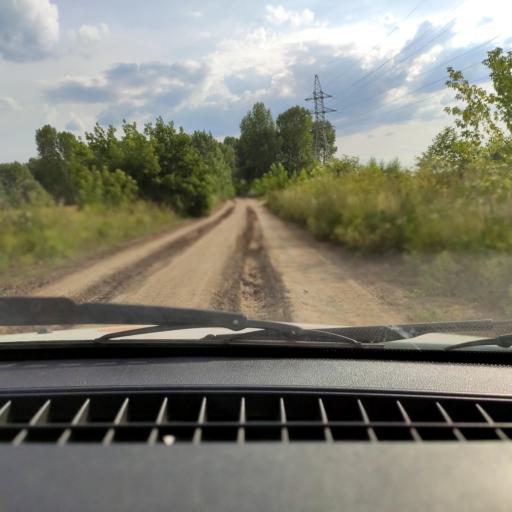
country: RU
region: Bashkortostan
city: Mikhaylovka
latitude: 54.9196
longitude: 55.9331
